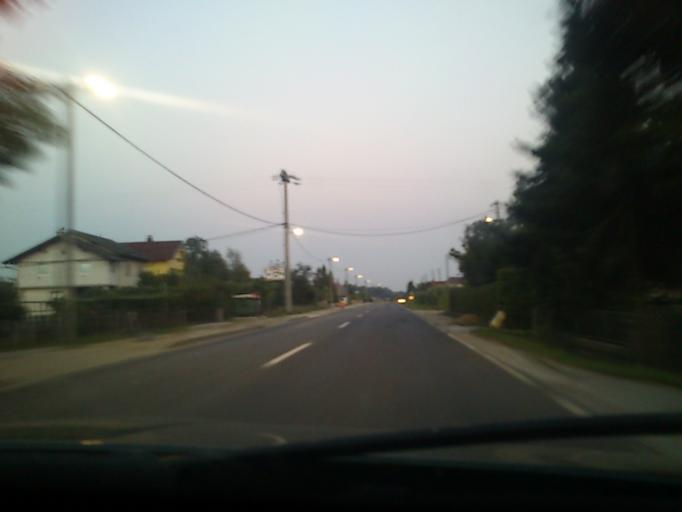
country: SI
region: Starse
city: Starse
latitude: 46.4758
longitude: 15.7485
